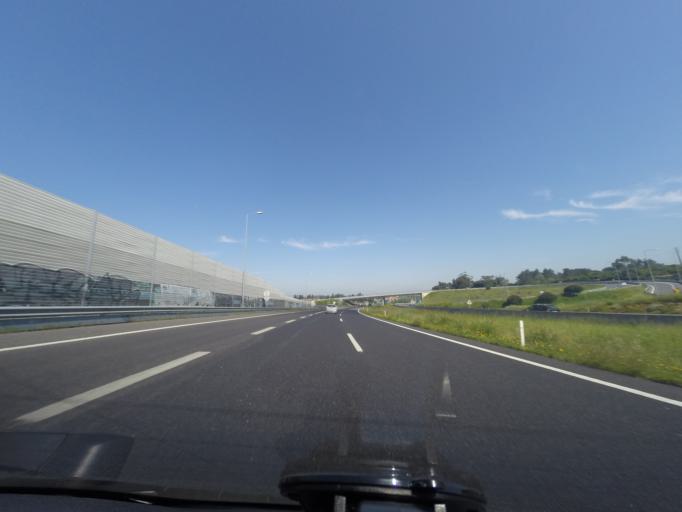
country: PT
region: Lisbon
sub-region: Sintra
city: Cacem
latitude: 38.7899
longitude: -9.3044
